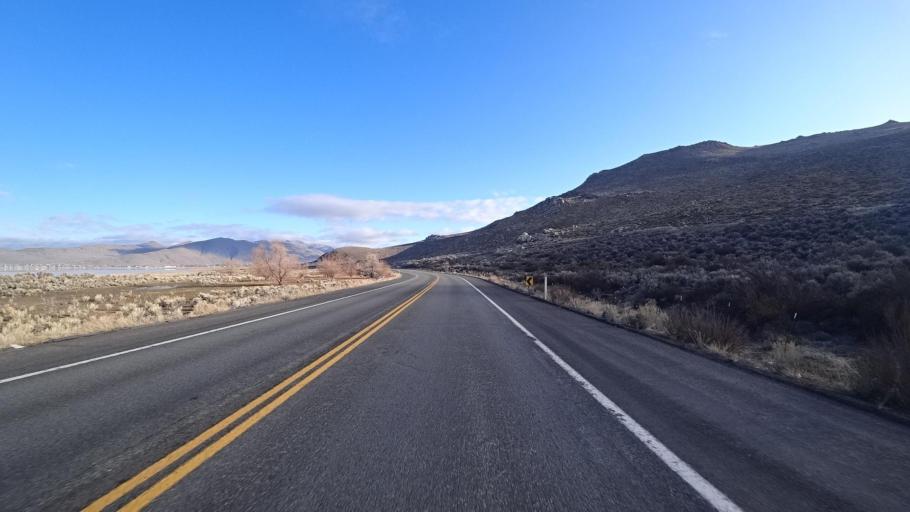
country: US
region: Nevada
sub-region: Washoe County
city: Cold Springs
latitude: 39.6527
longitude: -119.9588
